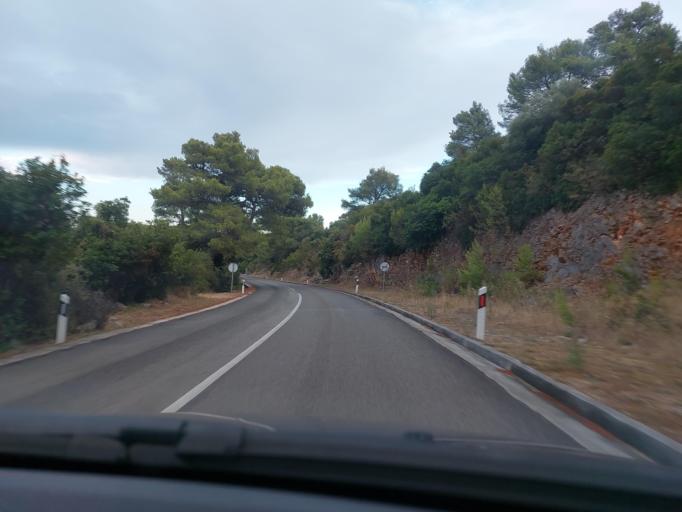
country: HR
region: Dubrovacko-Neretvanska
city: Smokvica
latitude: 42.7697
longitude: 16.8625
